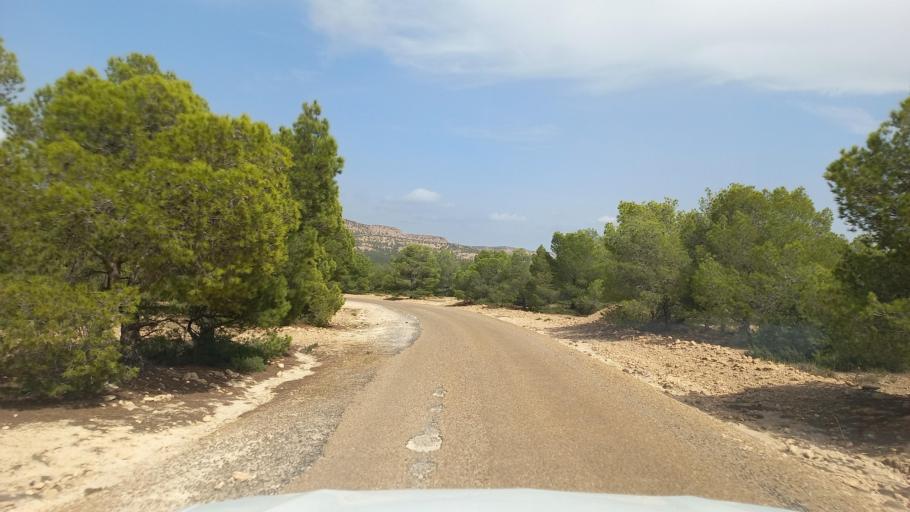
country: TN
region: Al Qasrayn
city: Sbiba
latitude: 35.4061
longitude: 8.9243
